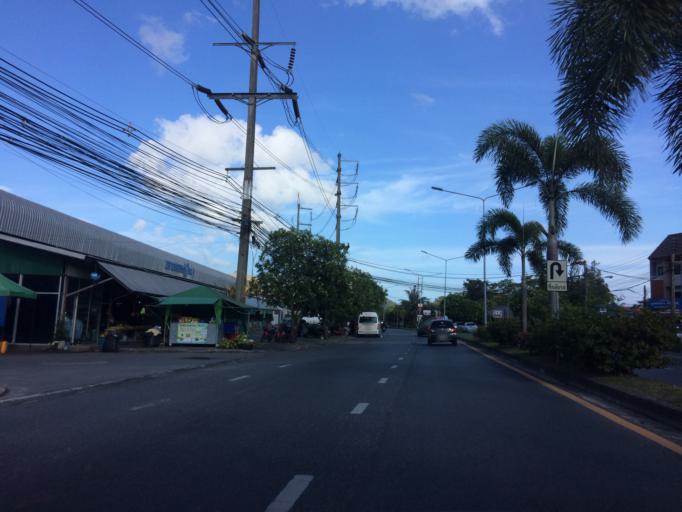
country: TH
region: Phuket
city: Kathu
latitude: 7.9071
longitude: 98.3493
